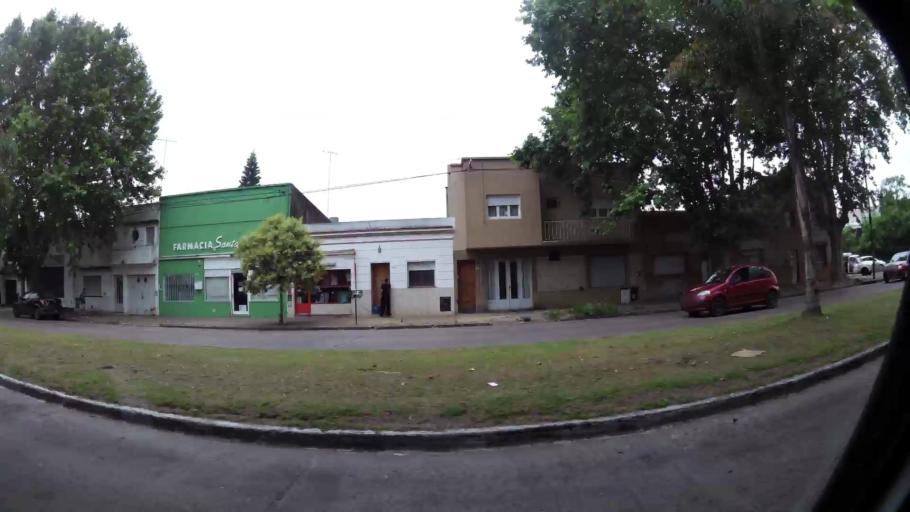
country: AR
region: Buenos Aires
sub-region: Partido de La Plata
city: La Plata
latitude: -34.9389
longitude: -57.9536
